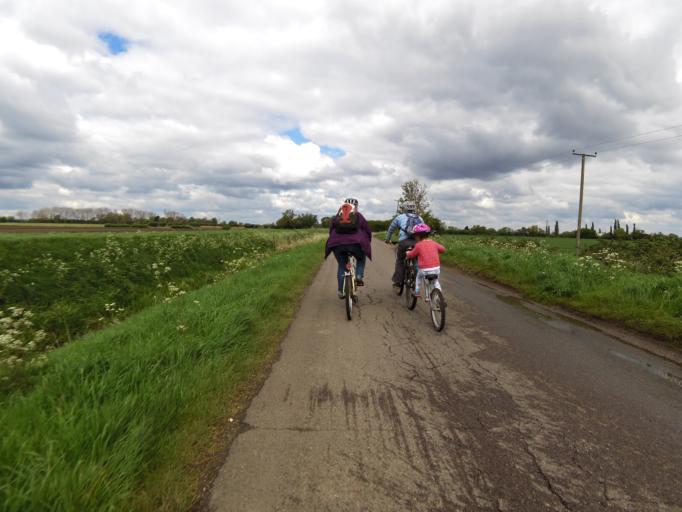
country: GB
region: England
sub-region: Cambridgeshire
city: Bottisham
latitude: 52.2490
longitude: 0.2373
